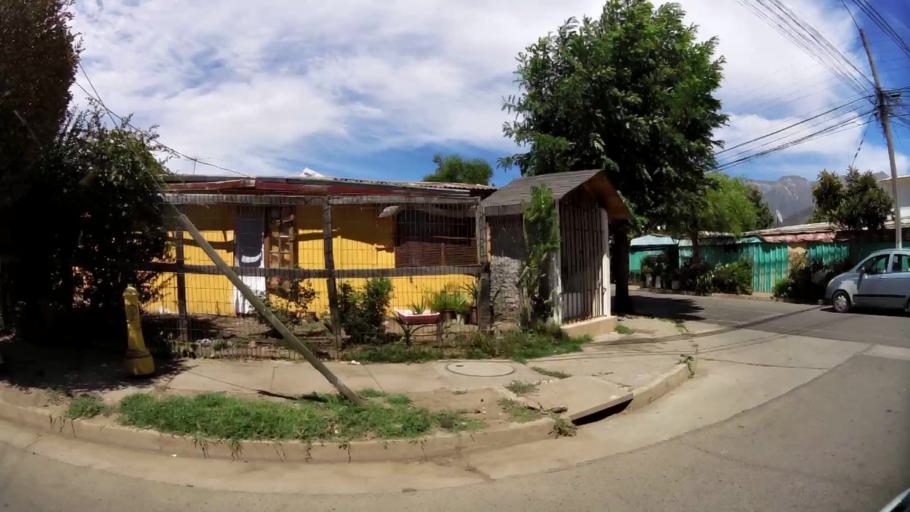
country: CL
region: O'Higgins
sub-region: Provincia de Cachapoal
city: Graneros
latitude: -33.9858
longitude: -70.7054
